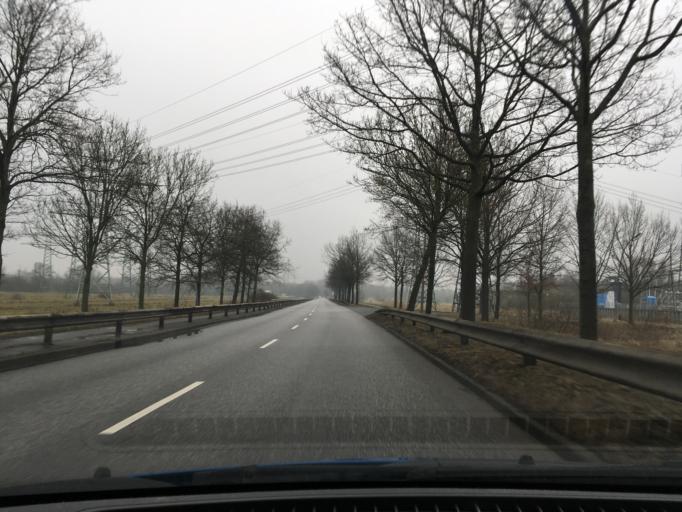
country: DE
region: Hamburg
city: Altona
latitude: 53.4888
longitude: 9.9063
